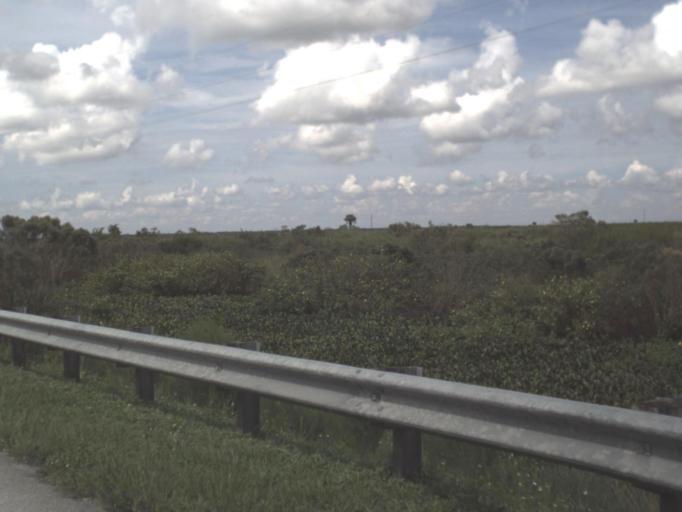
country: US
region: Florida
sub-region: Highlands County
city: Lake Placid
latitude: 27.2089
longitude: -81.2274
